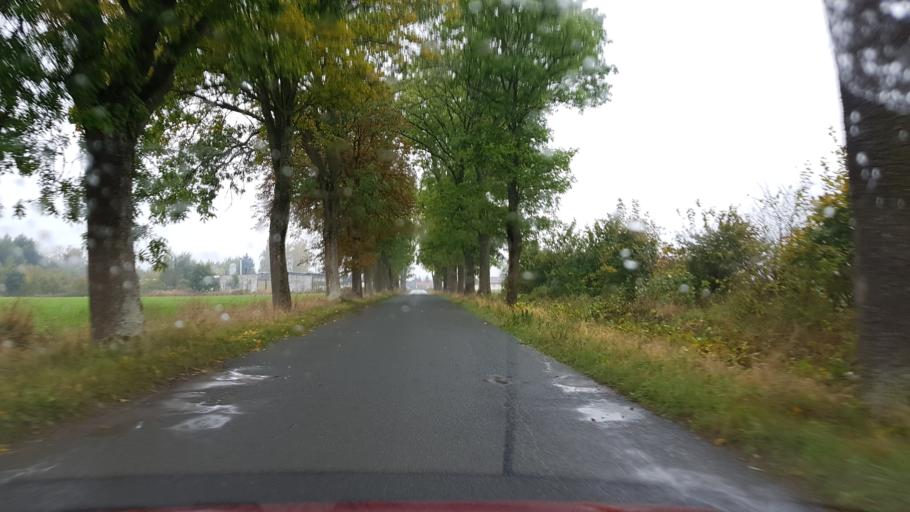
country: PL
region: Greater Poland Voivodeship
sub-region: Powiat zlotowski
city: Tarnowka
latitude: 53.3416
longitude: 16.8658
